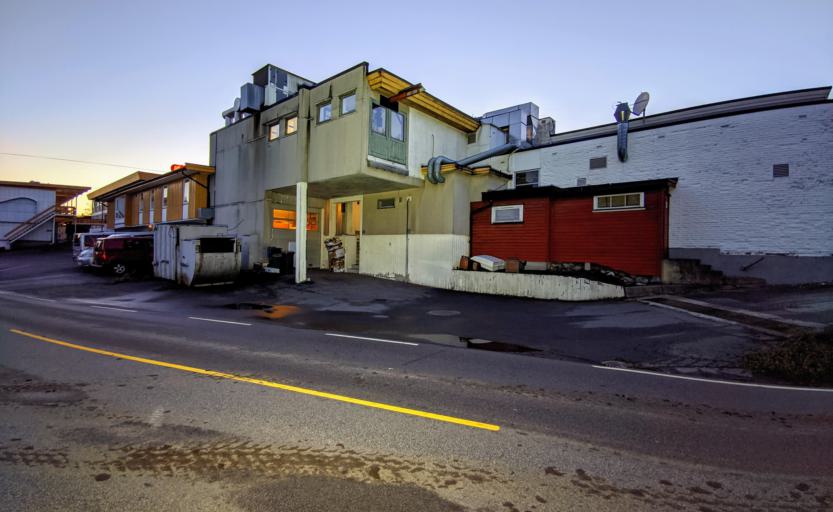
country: NO
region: Vestfold
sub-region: Larvik
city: Larvik
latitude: 59.1061
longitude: 10.1141
